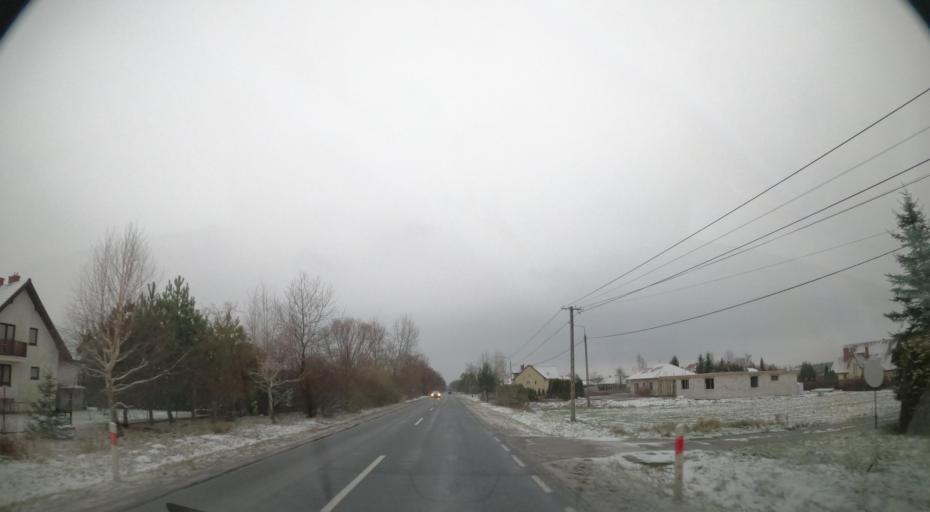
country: PL
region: Masovian Voivodeship
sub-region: Powiat plocki
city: Maszewo Duze
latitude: 52.5714
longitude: 19.6025
